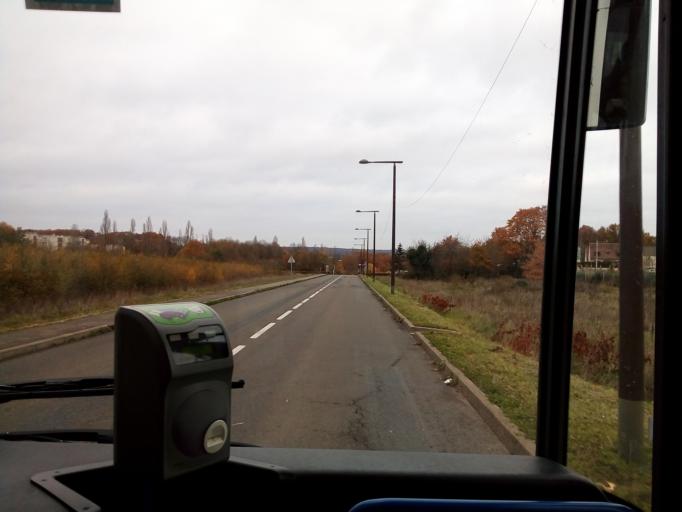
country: FR
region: Ile-de-France
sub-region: Departement de l'Essonne
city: Villebon-sur-Yvette
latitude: 48.7198
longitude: 2.2320
